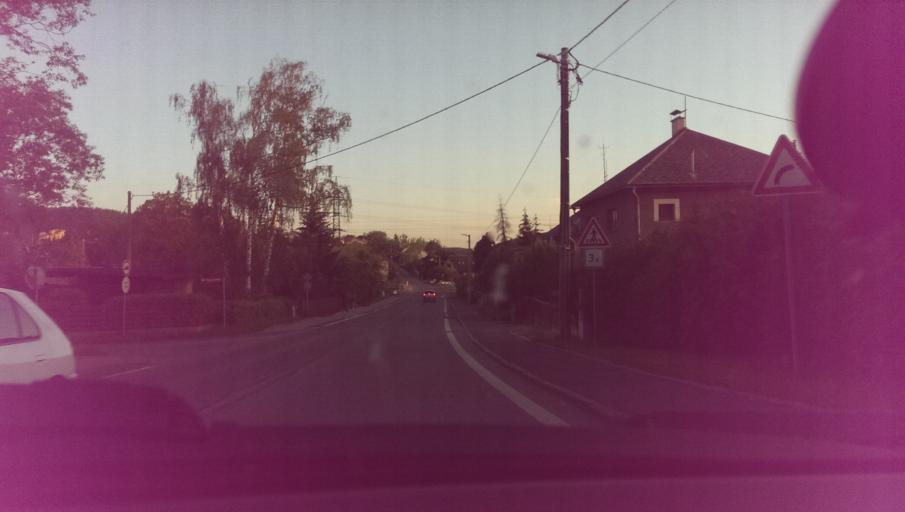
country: CZ
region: Zlin
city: Valasske Mezirici
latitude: 49.4613
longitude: 17.9746
